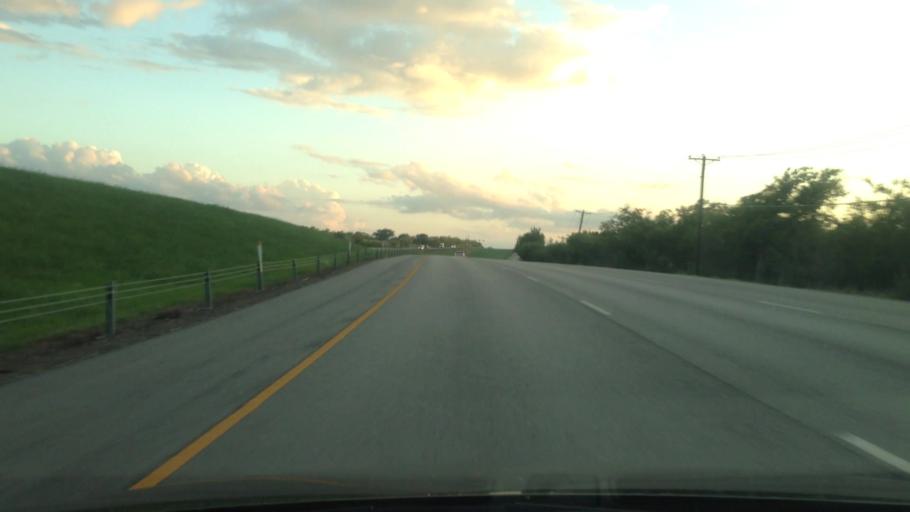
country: US
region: Texas
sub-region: Tarrant County
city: Benbrook
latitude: 32.6558
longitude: -97.4951
